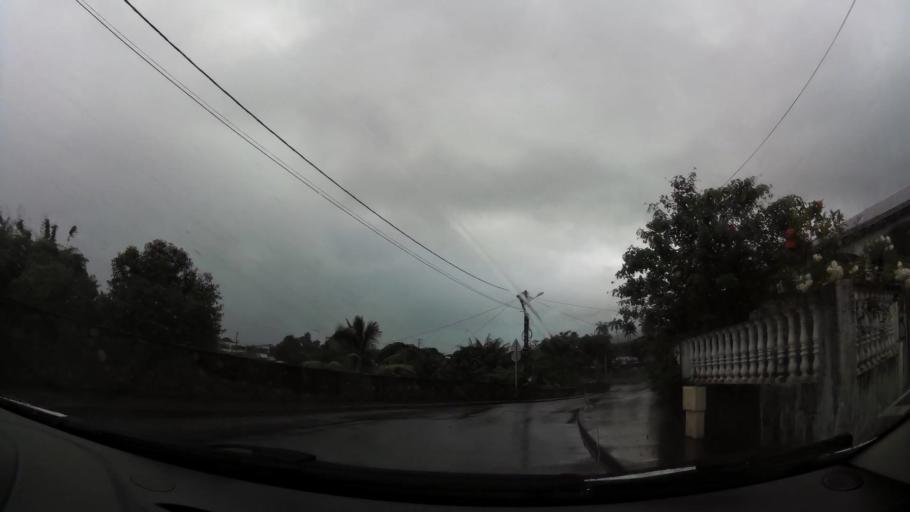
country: RE
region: Reunion
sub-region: Reunion
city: Bras-Panon
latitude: -21.0288
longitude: 55.6872
